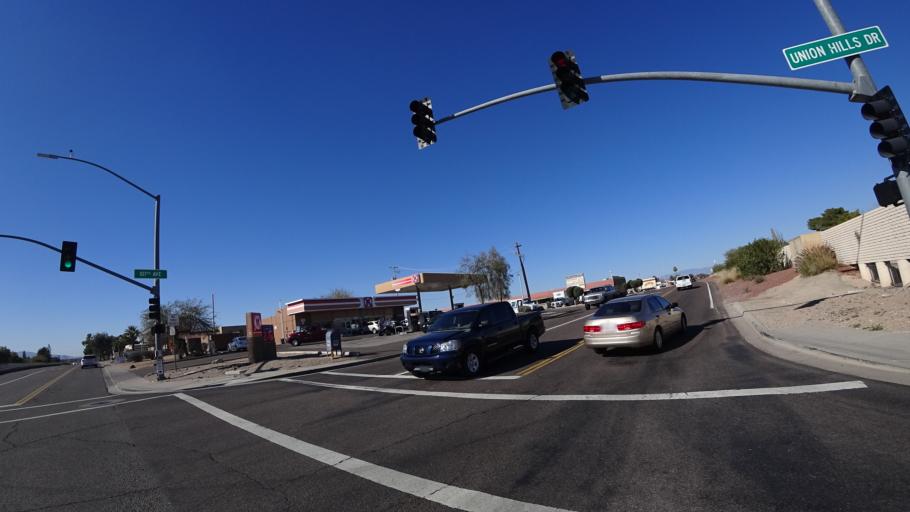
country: US
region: Arizona
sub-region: Maricopa County
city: Surprise
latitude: 33.6527
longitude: -112.2896
